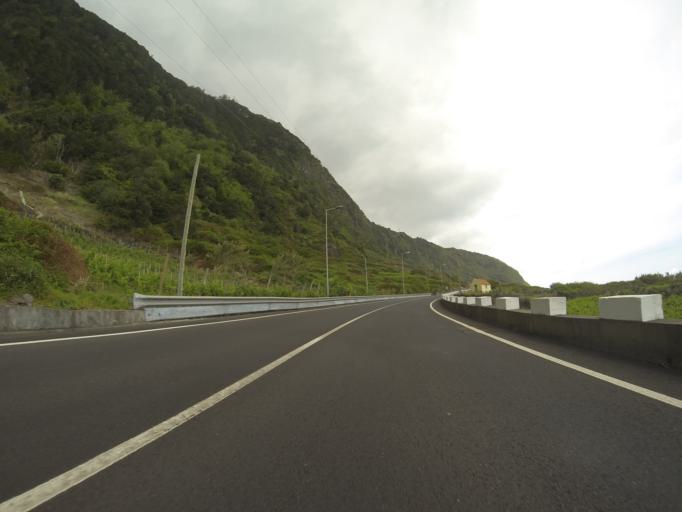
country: PT
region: Madeira
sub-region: Porto Moniz
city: Porto Moniz
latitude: 32.8448
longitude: -17.1459
